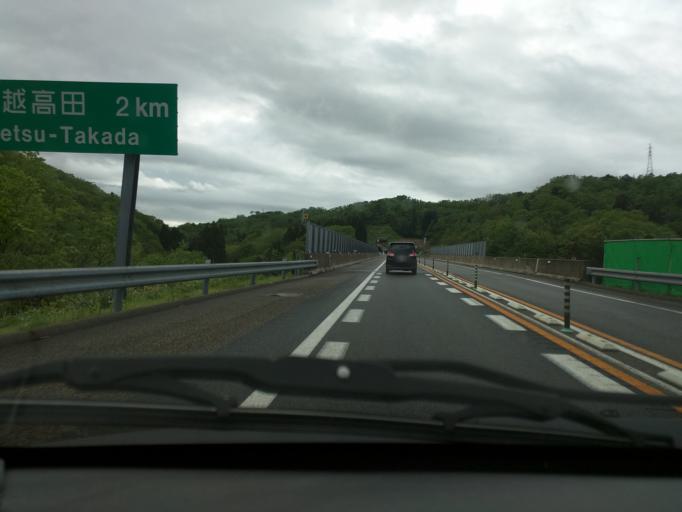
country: JP
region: Niigata
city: Joetsu
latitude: 37.1110
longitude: 138.2189
